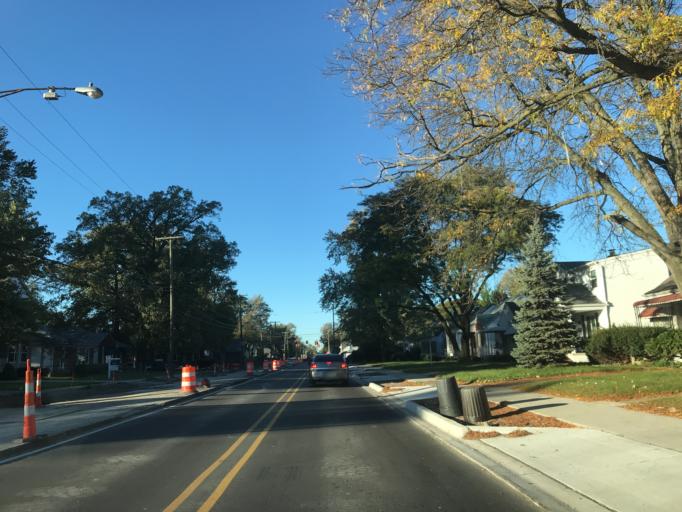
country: US
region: Michigan
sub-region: Oakland County
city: Madison Heights
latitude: 42.4858
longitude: -83.1242
